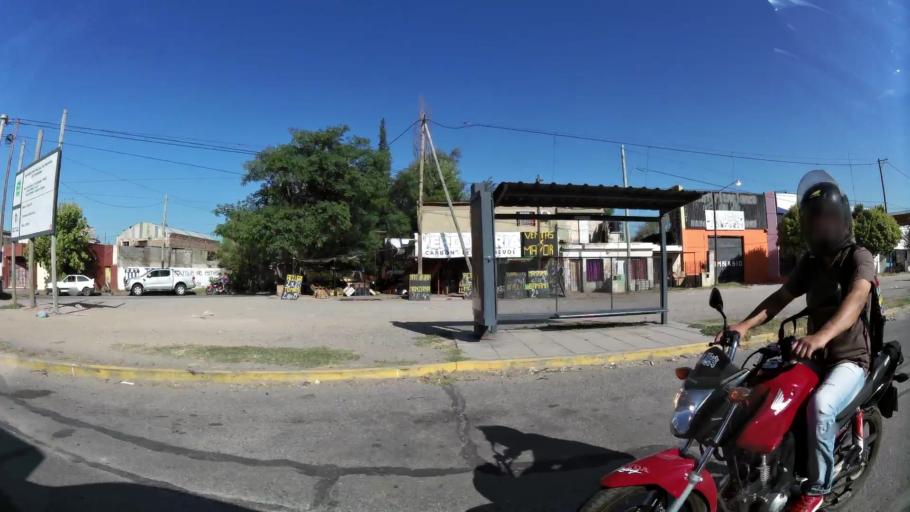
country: AR
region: Cordoba
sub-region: Departamento de Capital
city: Cordoba
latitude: -31.4698
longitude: -64.2275
